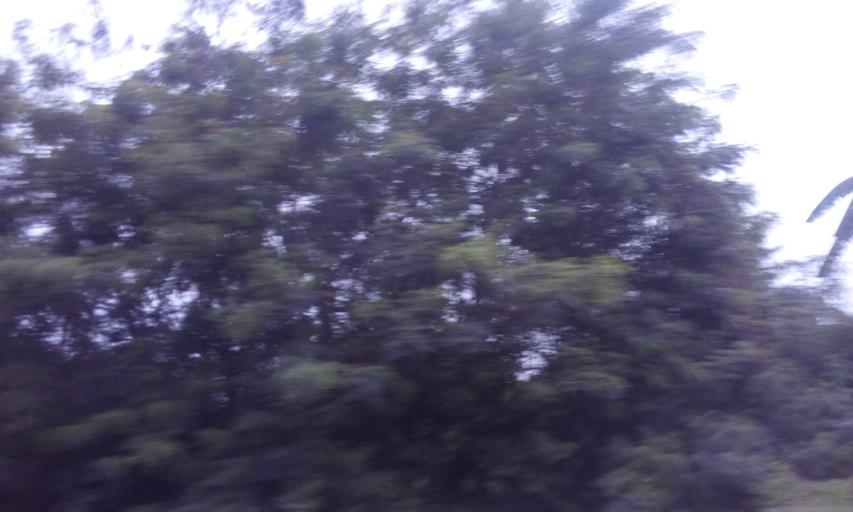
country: TH
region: Chachoengsao
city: Plaeng Yao
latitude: 13.5858
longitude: 101.2166
